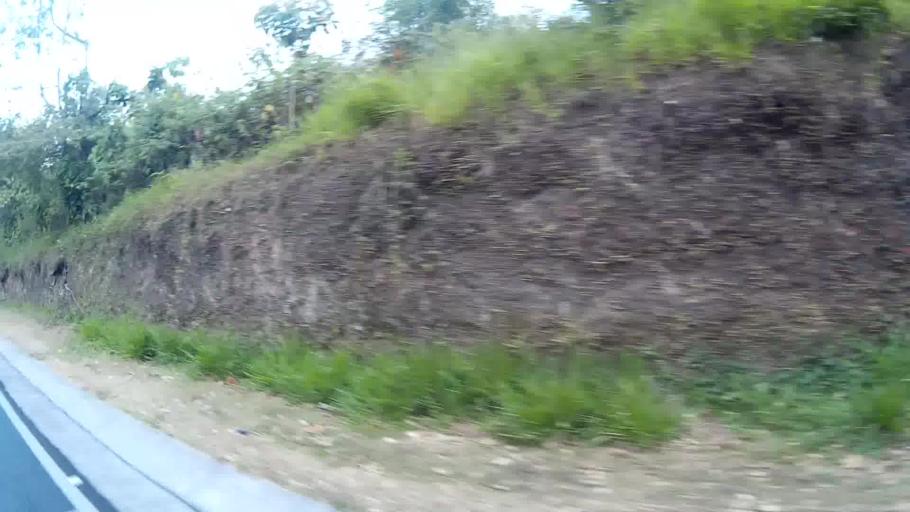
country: CO
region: Risaralda
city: Pereira
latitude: 4.7585
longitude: -75.6810
